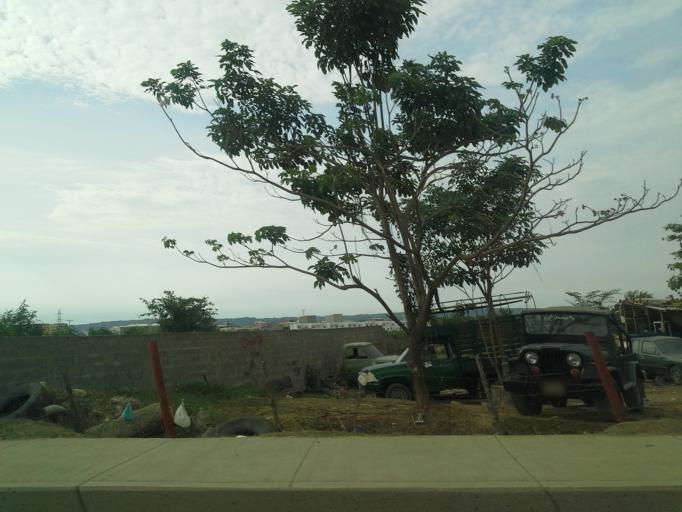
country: CO
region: Bolivar
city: Cartagena
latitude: 10.4006
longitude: -75.4659
